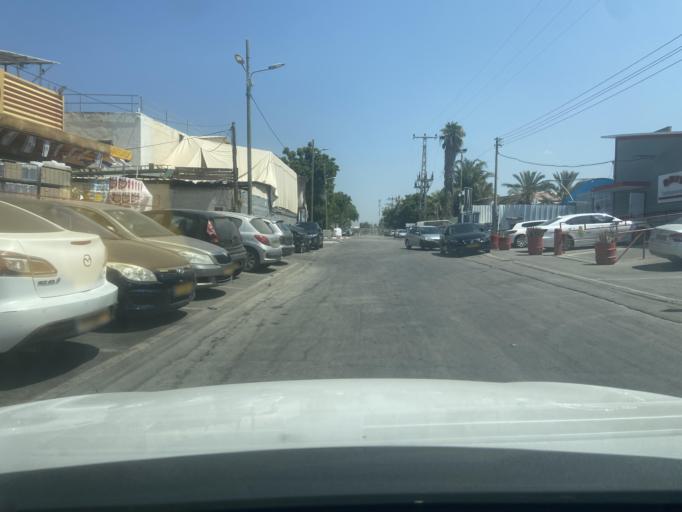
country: IL
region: Central District
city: Yehud
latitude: 32.0285
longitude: 34.9005
